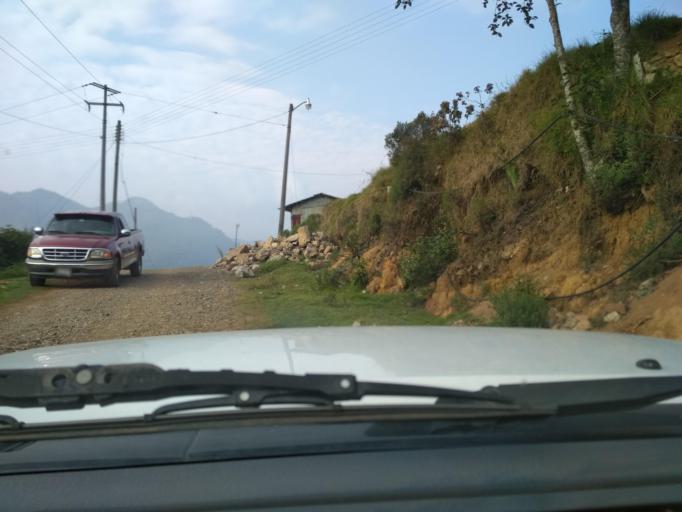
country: MX
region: Veracruz
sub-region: Soledad Atzompa
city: Tlatilpa
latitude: 18.7542
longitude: -97.1574
